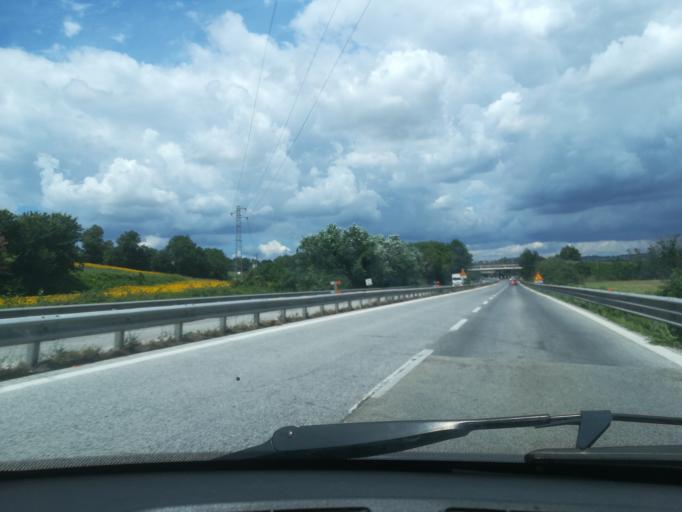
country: IT
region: The Marches
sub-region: Provincia di Macerata
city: Corridonia
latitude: 43.2663
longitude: 13.5263
